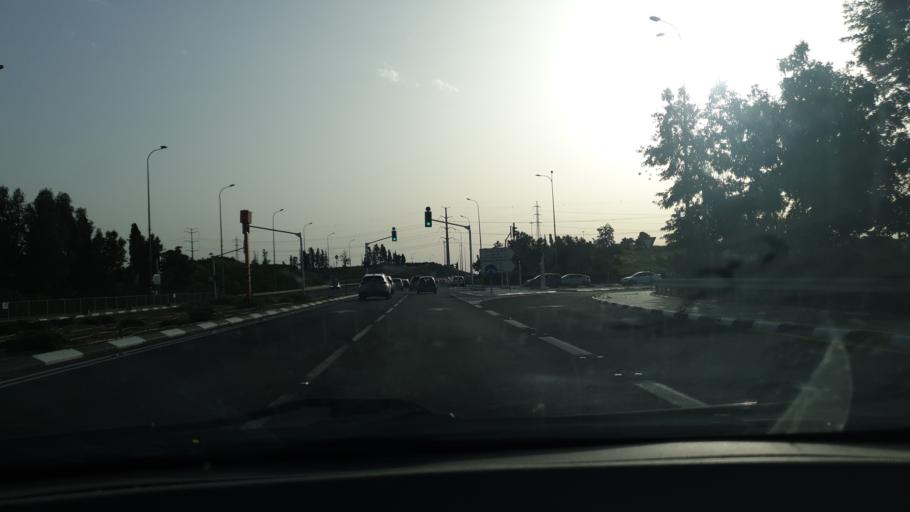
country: IL
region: Central District
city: Even Yehuda
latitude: 32.2580
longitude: 34.9000
